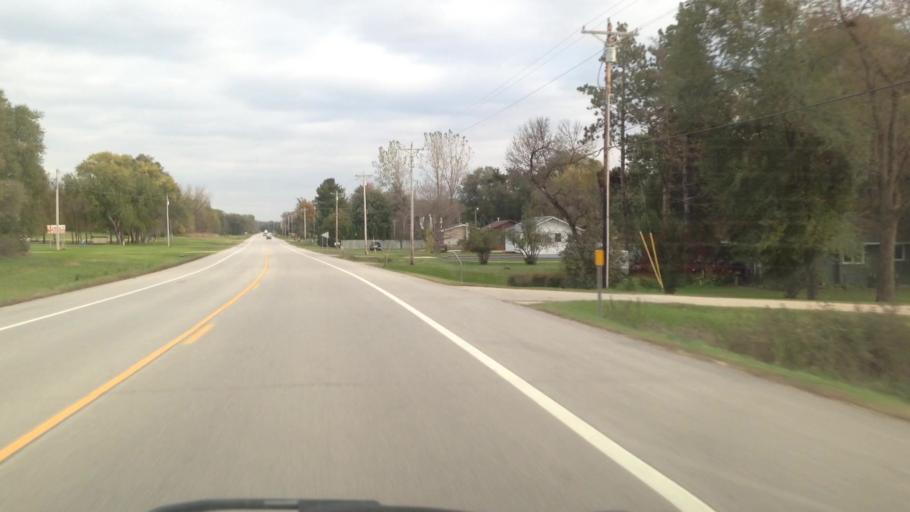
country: US
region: Minnesota
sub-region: Olmsted County
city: Rochester
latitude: 43.9729
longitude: -92.3912
